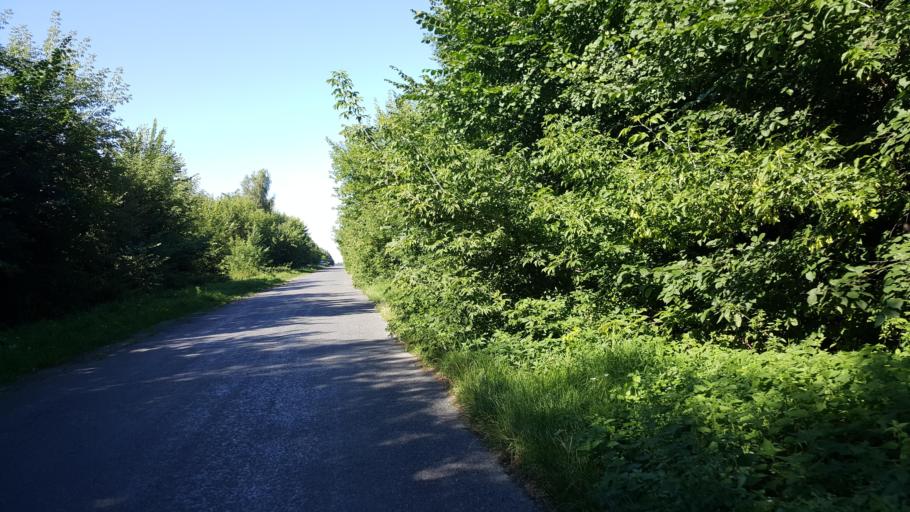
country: BY
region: Brest
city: Charnawchytsy
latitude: 52.2360
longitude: 23.7445
